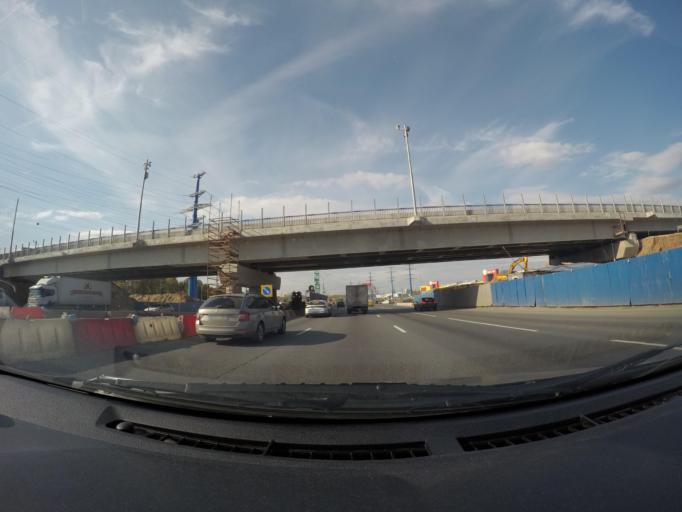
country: RU
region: Moscow
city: Lianozovo
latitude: 55.9098
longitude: 37.5893
